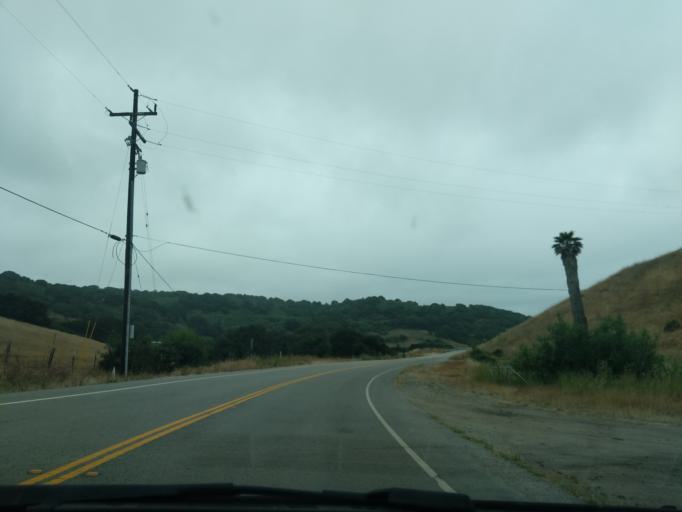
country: US
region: California
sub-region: San Benito County
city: Aromas
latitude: 36.8629
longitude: -121.6223
